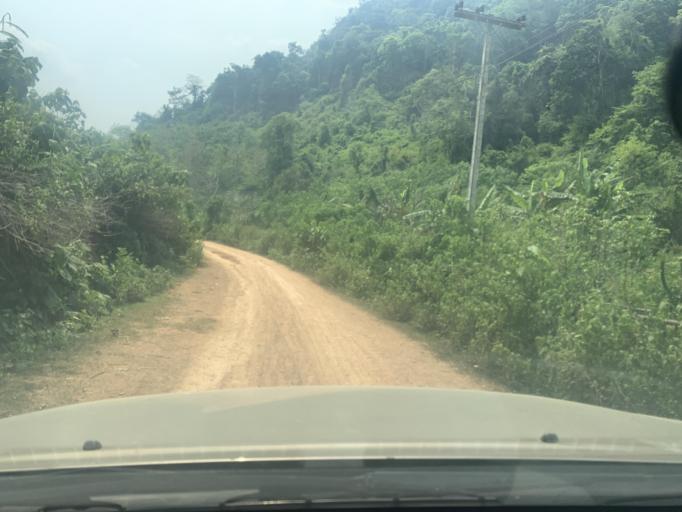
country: LA
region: Louangphabang
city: Louangphabang
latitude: 19.9696
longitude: 102.1218
